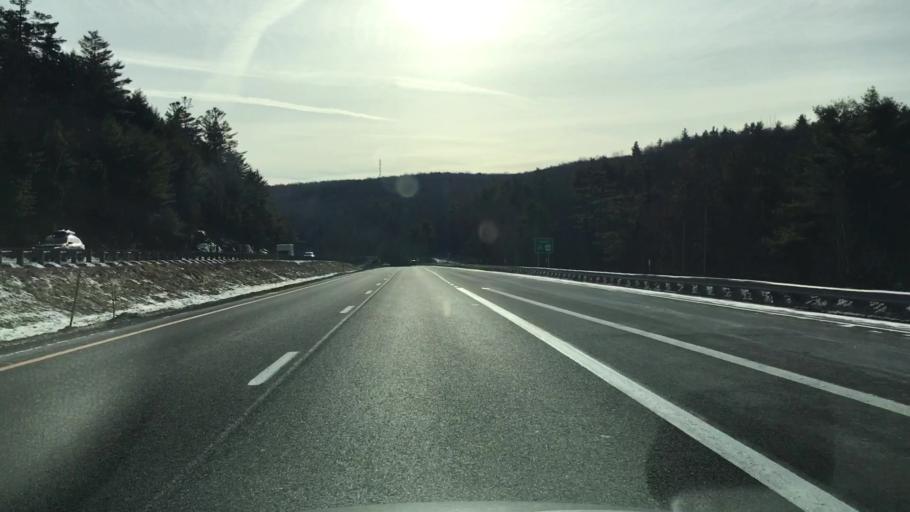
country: US
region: New Hampshire
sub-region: Grafton County
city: Enfield
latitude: 43.5944
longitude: -72.1664
